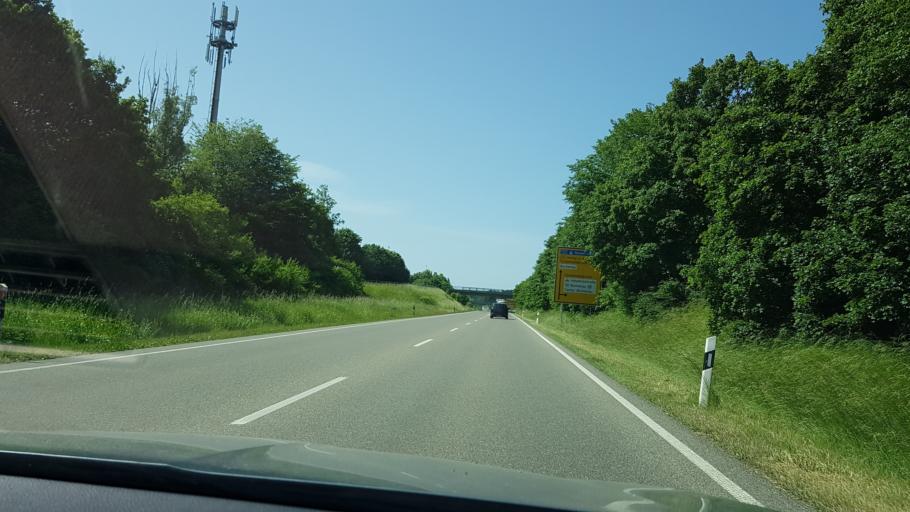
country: DE
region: Bavaria
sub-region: Upper Bavaria
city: Schongeising
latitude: 48.1649
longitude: 11.2204
